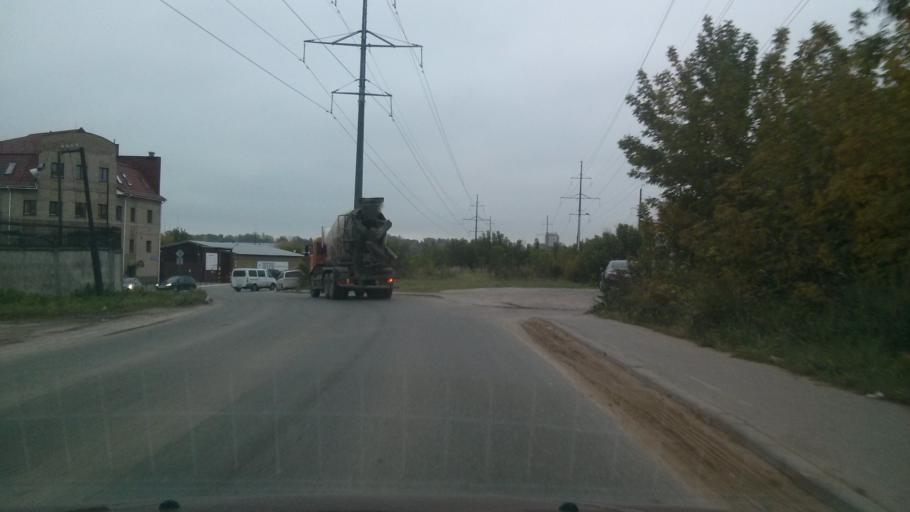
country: RU
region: Nizjnij Novgorod
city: Nizhniy Novgorod
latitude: 56.3027
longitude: 44.0096
